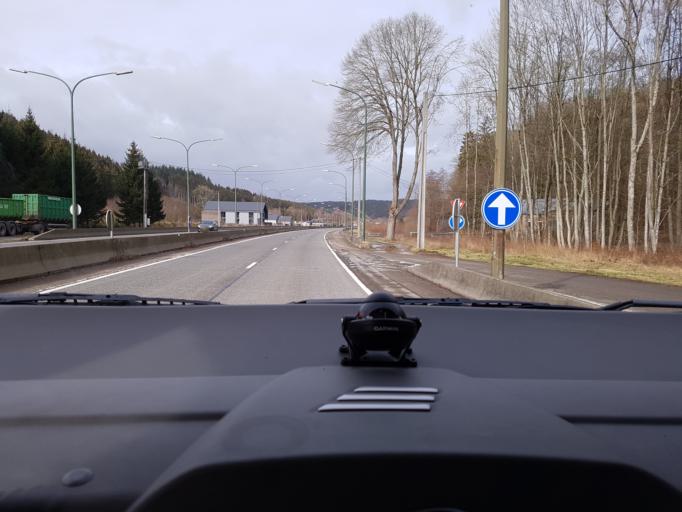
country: BE
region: Wallonia
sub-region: Province du Luxembourg
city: Nassogne
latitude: 50.1526
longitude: 5.4199
